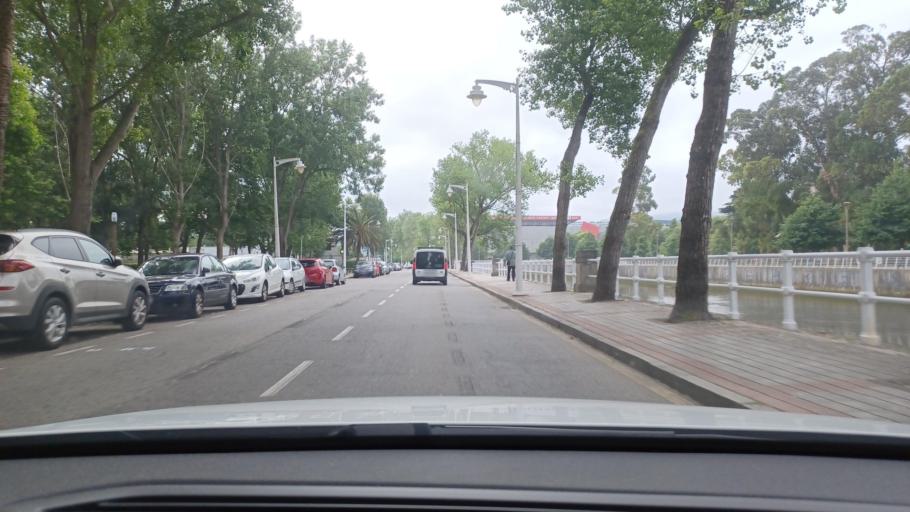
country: ES
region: Asturias
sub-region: Province of Asturias
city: Gijon
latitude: 43.5391
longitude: -5.6411
